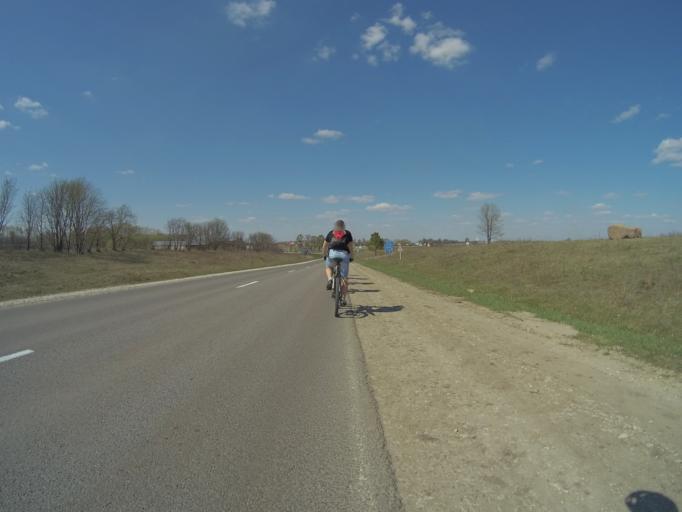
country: RU
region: Vladimir
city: Suzdal'
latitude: 56.4000
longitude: 40.4479
